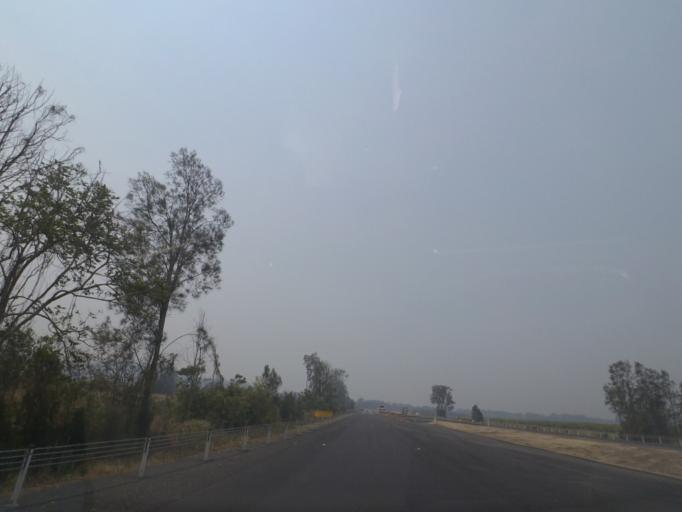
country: AU
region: New South Wales
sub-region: Ballina
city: Ballina
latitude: -28.8749
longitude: 153.4892
